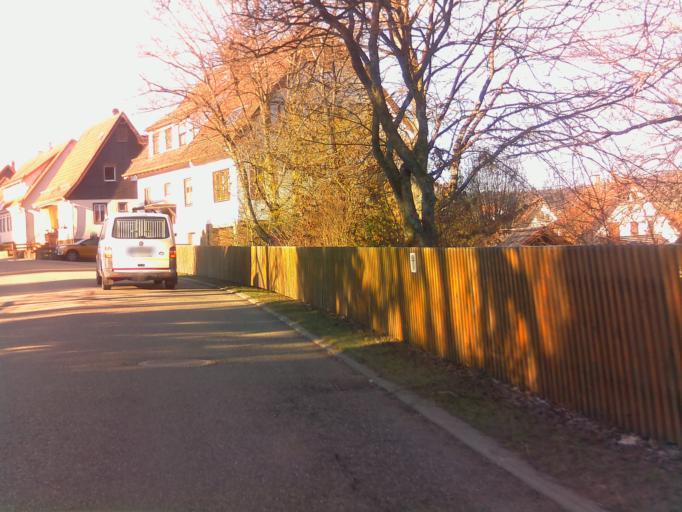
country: DE
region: Baden-Wuerttemberg
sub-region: Karlsruhe Region
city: Oberreichenbach
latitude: 48.7247
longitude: 8.6307
